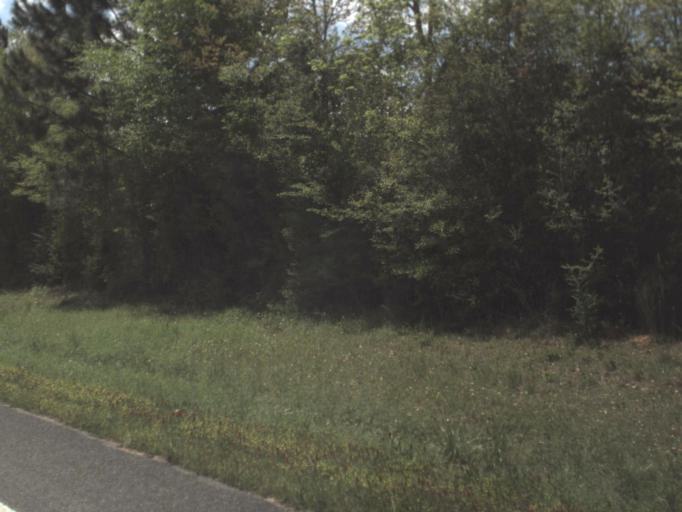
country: US
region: Florida
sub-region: Okaloosa County
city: Crestview
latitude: 30.8839
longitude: -86.6636
